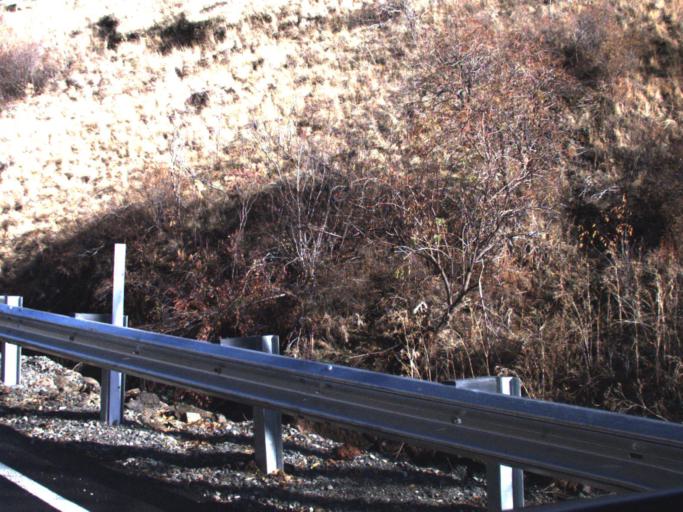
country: US
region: Washington
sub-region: Asotin County
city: Asotin
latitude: 46.0529
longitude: -117.2392
